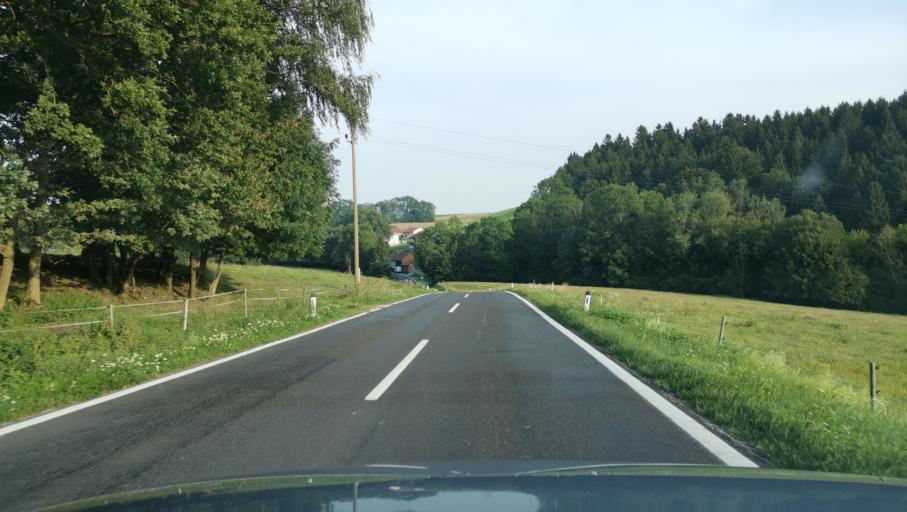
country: DE
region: Bavaria
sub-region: Lower Bavaria
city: Obernzell
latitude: 48.3662
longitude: 13.6666
